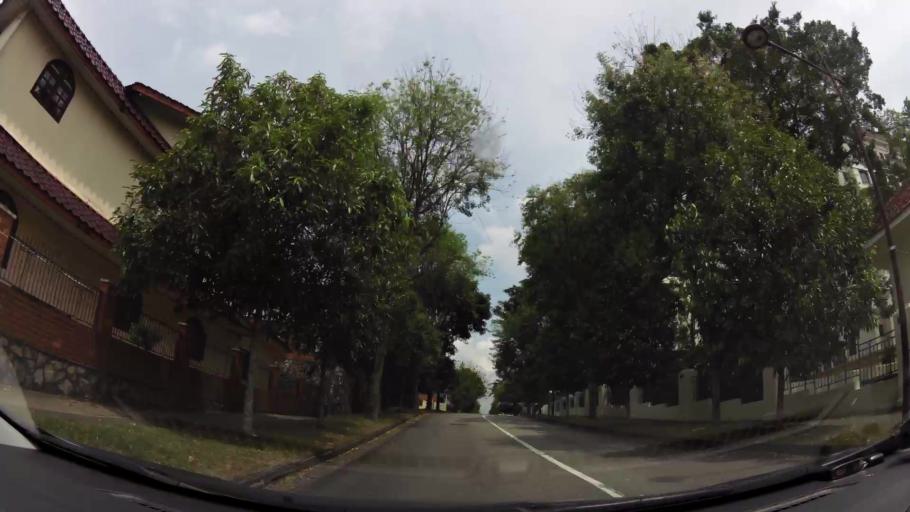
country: MY
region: Johor
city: Johor Bahru
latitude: 1.3583
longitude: 103.7616
